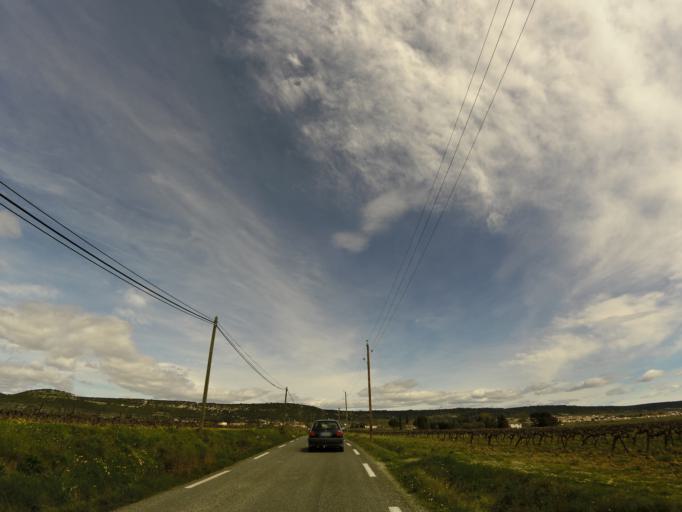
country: FR
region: Languedoc-Roussillon
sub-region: Departement du Gard
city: Clarensac
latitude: 43.8141
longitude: 4.2001
